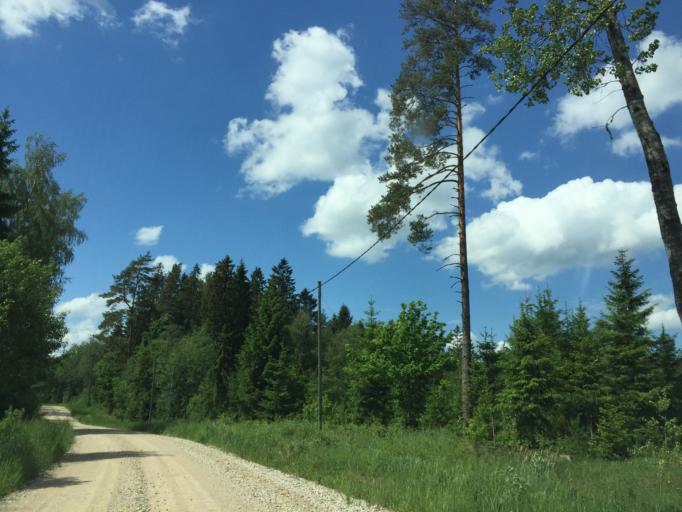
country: LV
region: Priekuli
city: Priekuli
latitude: 57.2303
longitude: 25.4316
